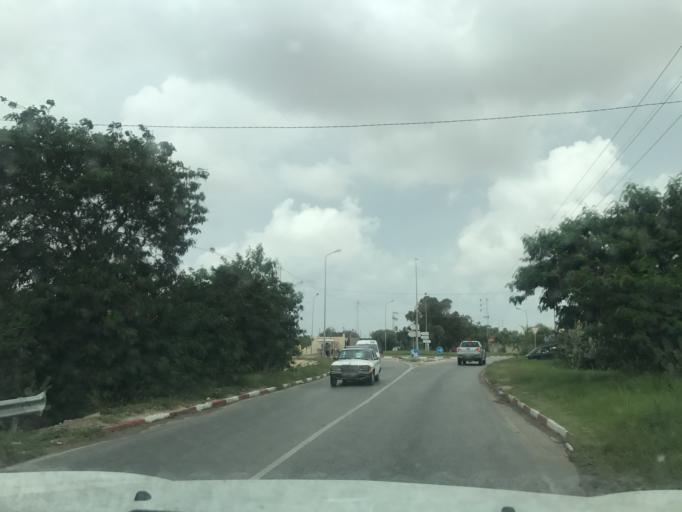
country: TN
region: Al Munastir
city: Qasr Hallal
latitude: 35.6017
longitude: 10.8994
